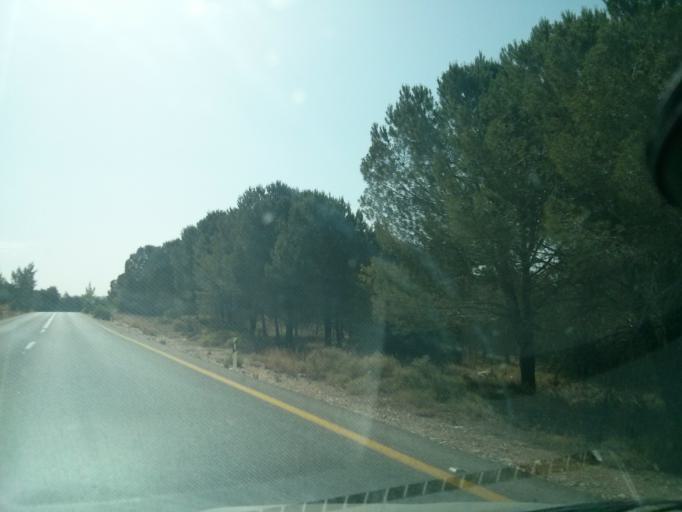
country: PS
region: West Bank
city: Surif
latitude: 31.6749
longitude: 35.0440
